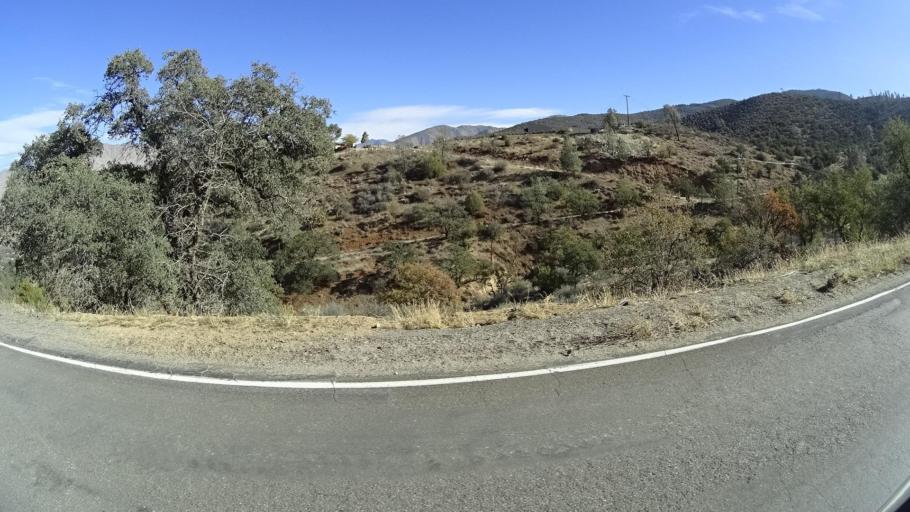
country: US
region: California
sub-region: Kern County
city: Bodfish
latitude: 35.5810
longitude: -118.5029
